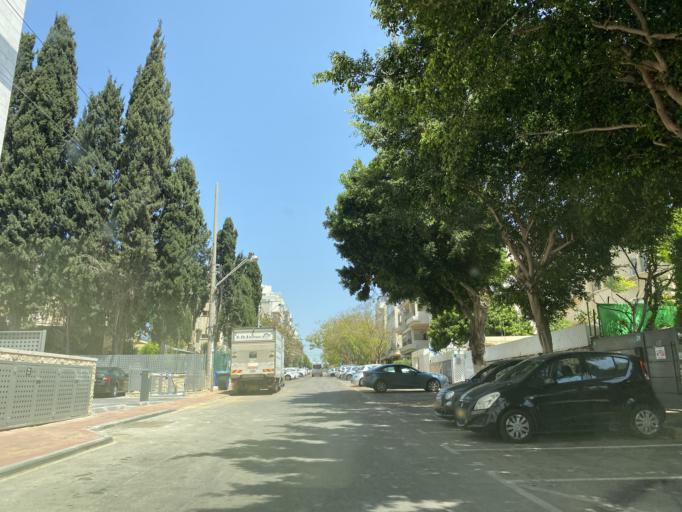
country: IL
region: Central District
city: Ra'anana
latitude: 32.1756
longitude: 34.8784
